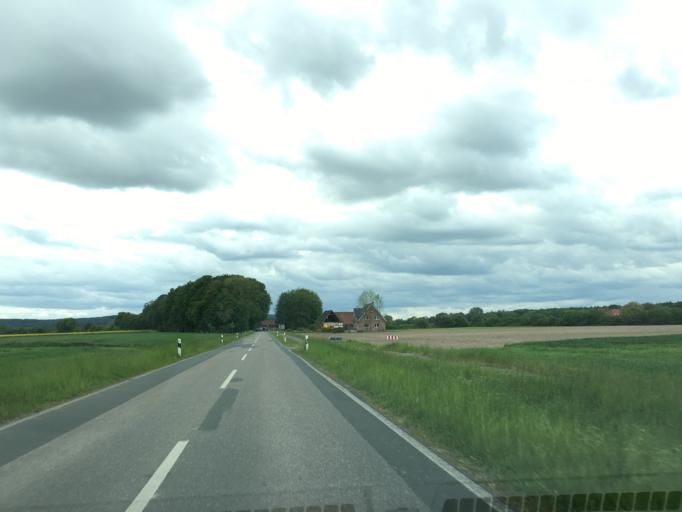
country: DE
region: North Rhine-Westphalia
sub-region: Regierungsbezirk Munster
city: Havixbeck
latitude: 51.9444
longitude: 7.4841
